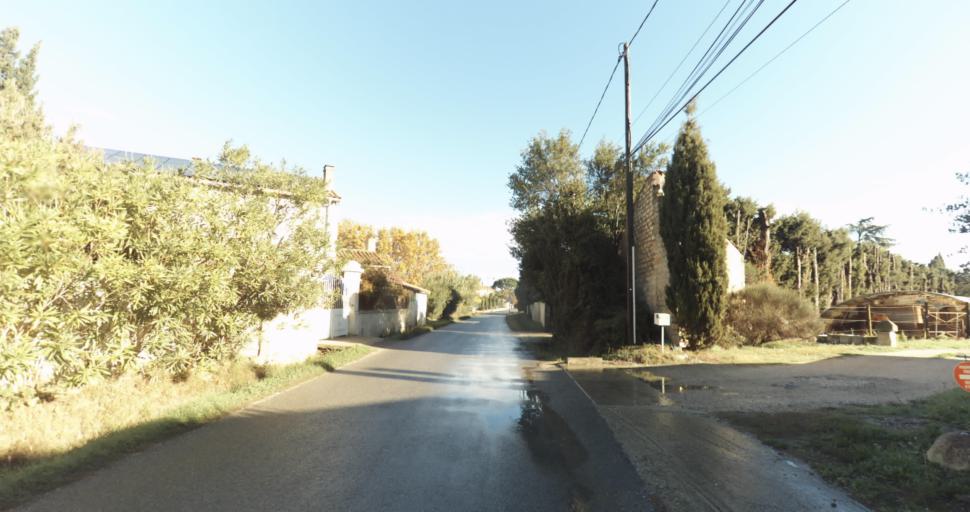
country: FR
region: Provence-Alpes-Cote d'Azur
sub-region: Departement des Bouches-du-Rhone
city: Rognonas
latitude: 43.8950
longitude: 4.7995
